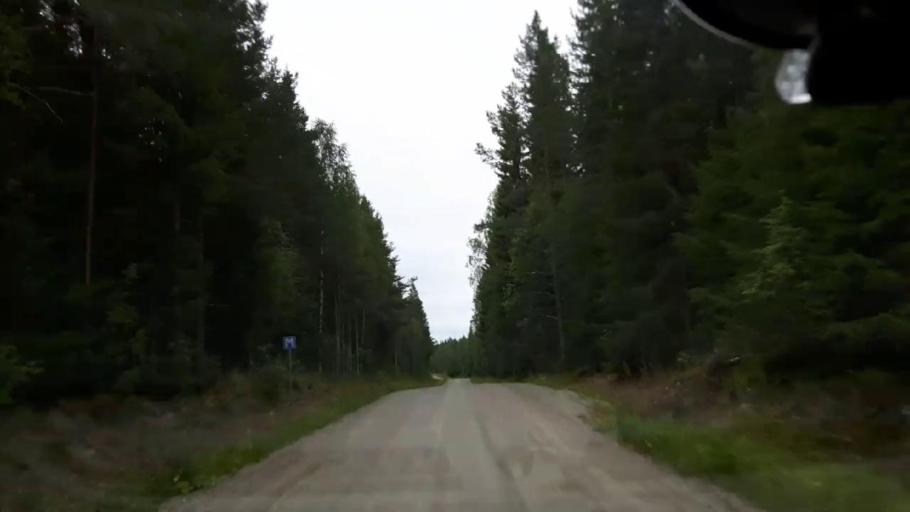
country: SE
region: Jaemtland
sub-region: Braecke Kommun
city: Braecke
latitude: 62.8251
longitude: 15.7100
